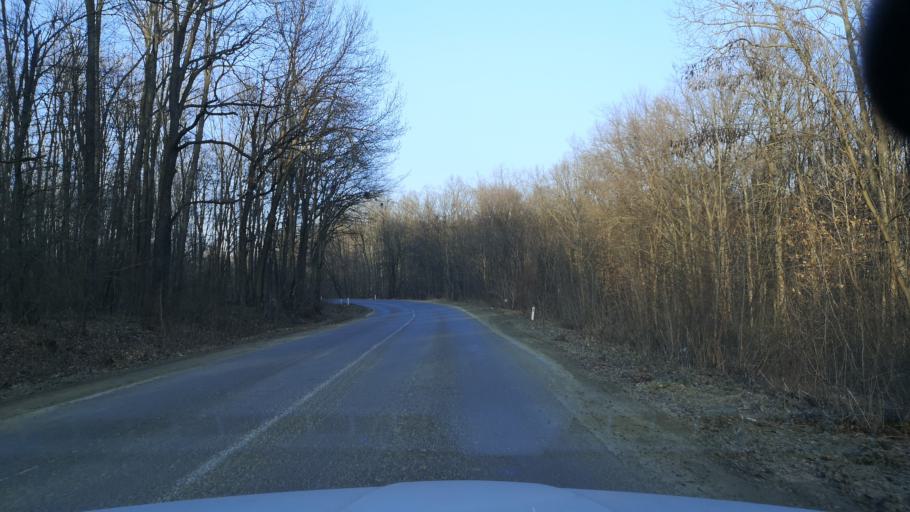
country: MD
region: Stinga Nistrului
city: Bucovat
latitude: 47.1319
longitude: 28.4995
